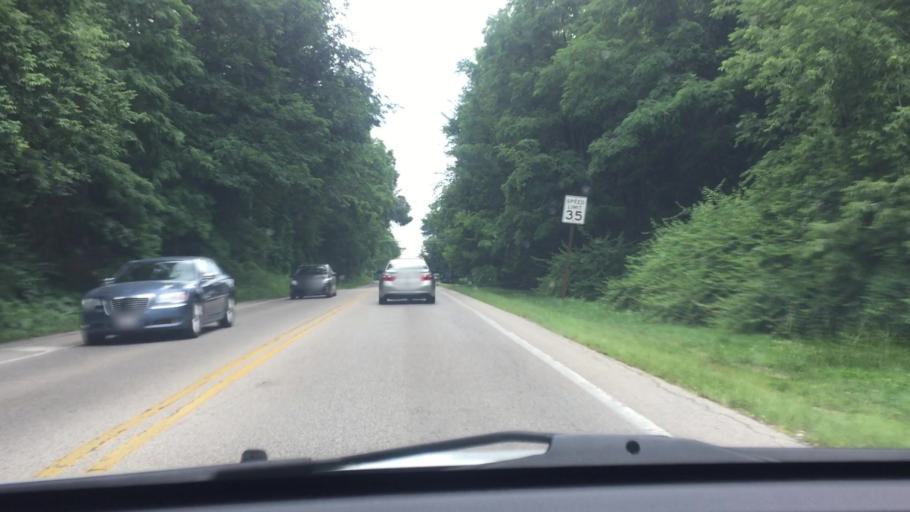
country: US
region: Wisconsin
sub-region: Waukesha County
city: Brookfield
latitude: 43.0605
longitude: -88.0973
